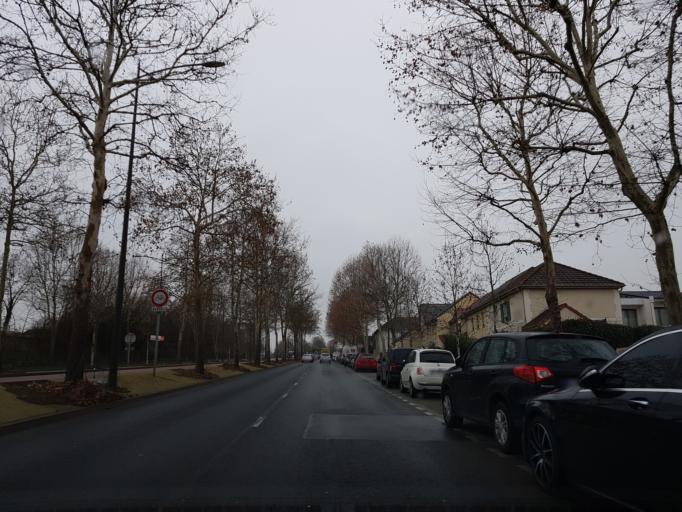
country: FR
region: Ile-de-France
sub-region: Departement du Val-de-Marne
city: Thiais
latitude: 48.7582
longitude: 2.3917
